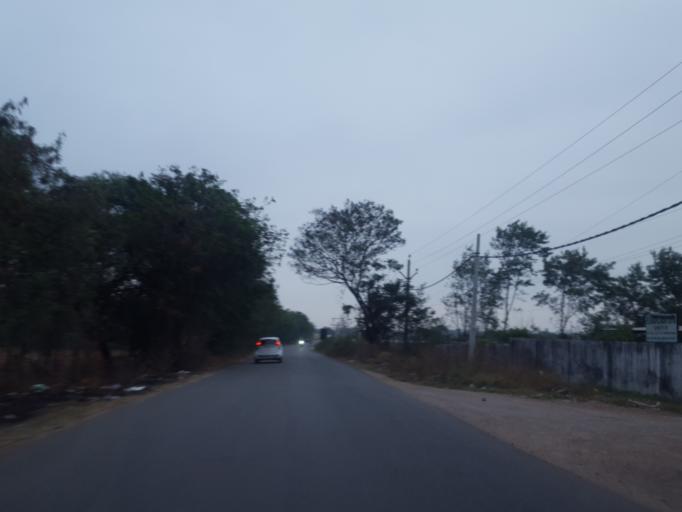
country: IN
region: Telangana
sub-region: Medak
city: Patancheru
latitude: 17.5060
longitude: 78.2041
